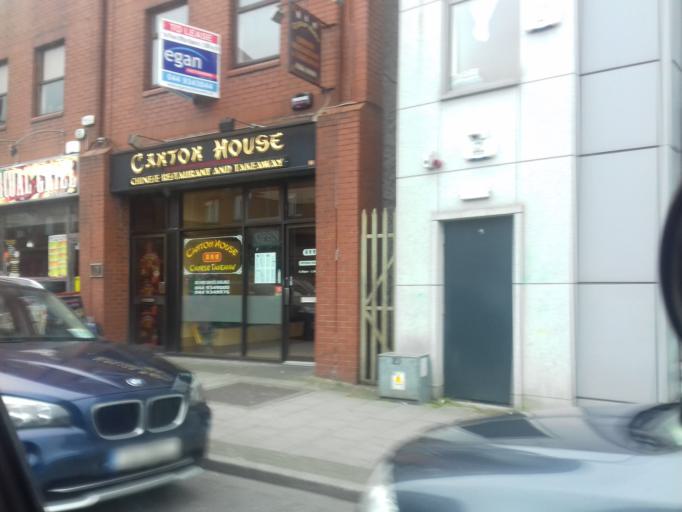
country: IE
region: Leinster
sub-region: An Iarmhi
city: An Muileann gCearr
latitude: 53.5264
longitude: -7.3398
